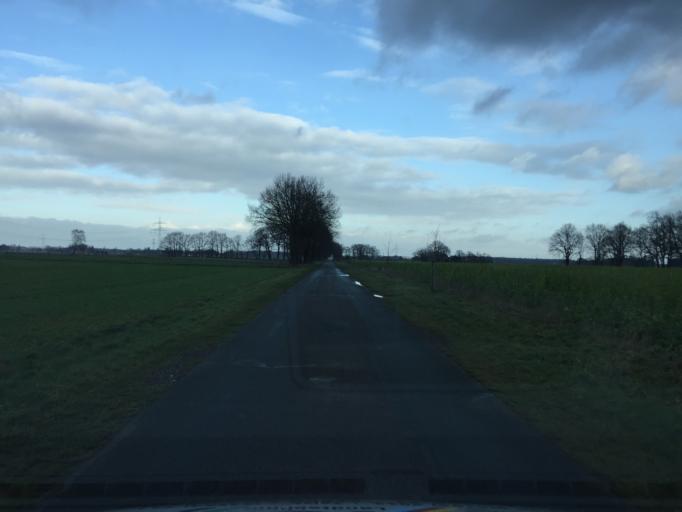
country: DE
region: Lower Saxony
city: Steyerberg
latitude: 52.5230
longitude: 9.0007
